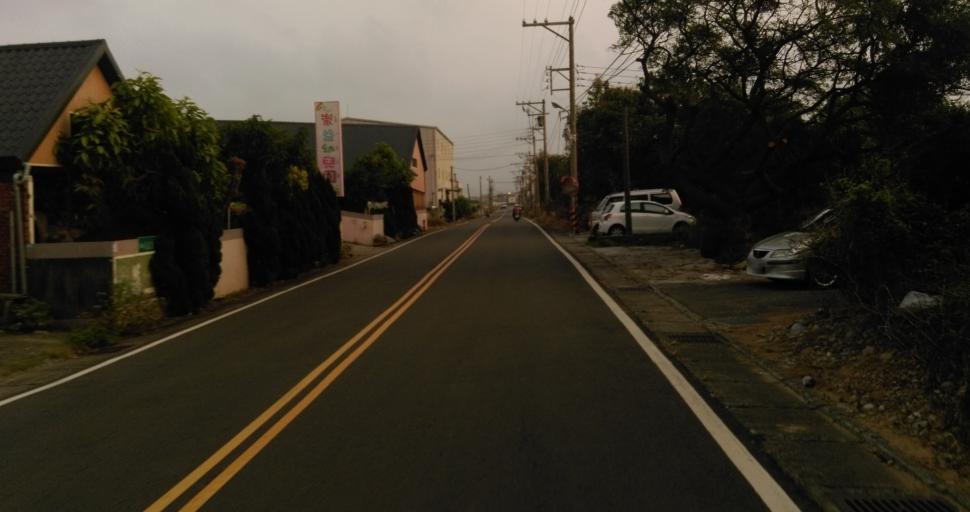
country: TW
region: Taiwan
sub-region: Hsinchu
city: Zhubei
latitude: 24.8758
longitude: 120.9551
